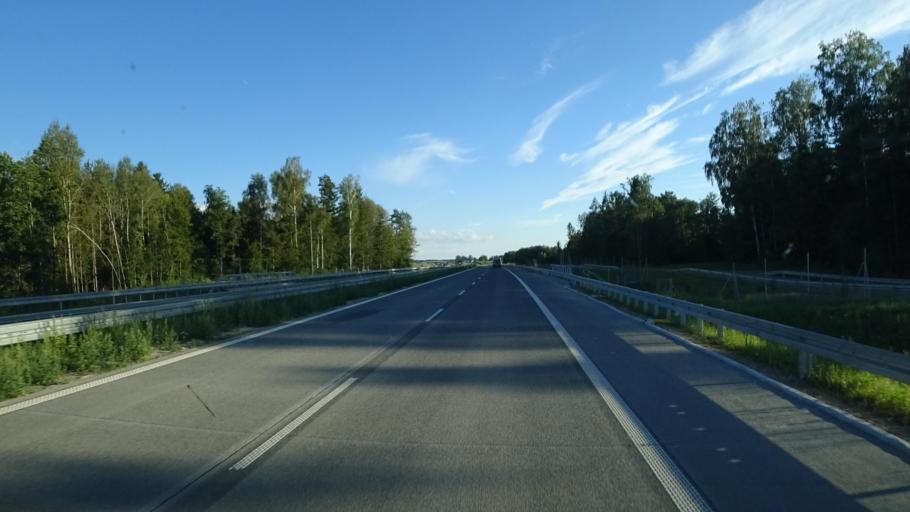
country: PL
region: Podlasie
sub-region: Powiat suwalski
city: Raczki
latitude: 53.9566
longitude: 22.7701
